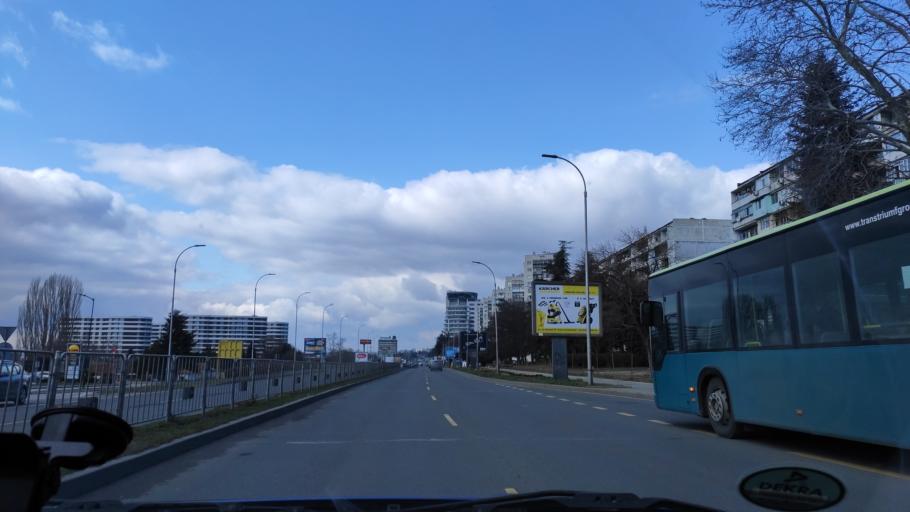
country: BG
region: Varna
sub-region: Obshtina Varna
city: Varna
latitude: 43.2203
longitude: 27.8842
